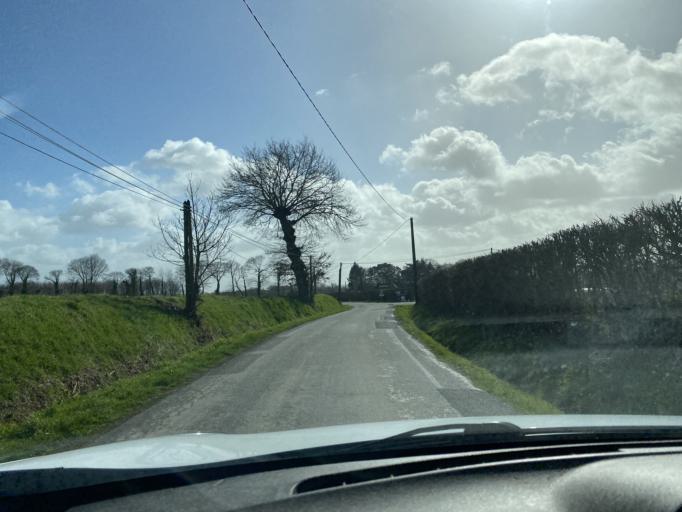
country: FR
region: Brittany
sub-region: Departement d'Ille-et-Vilaine
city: Melesse
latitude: 48.2103
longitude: -1.6859
